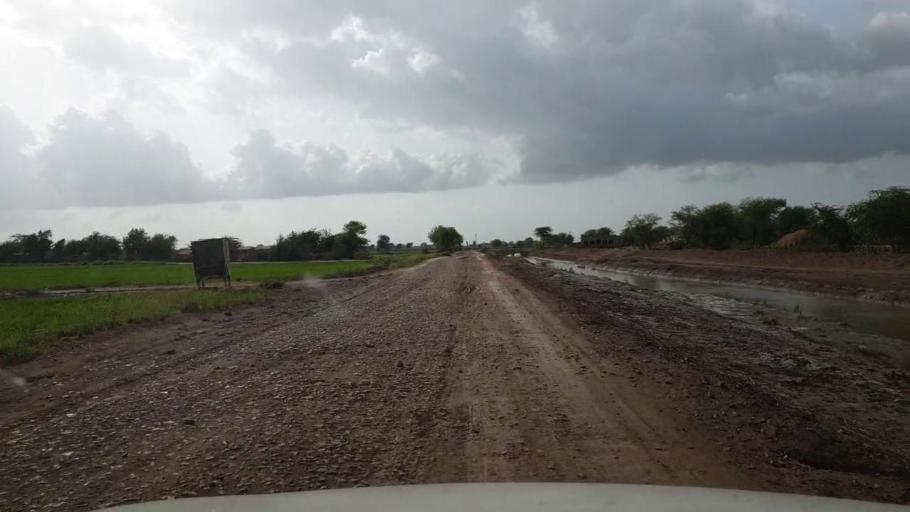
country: PK
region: Sindh
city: Kario
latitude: 24.7879
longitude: 68.5826
